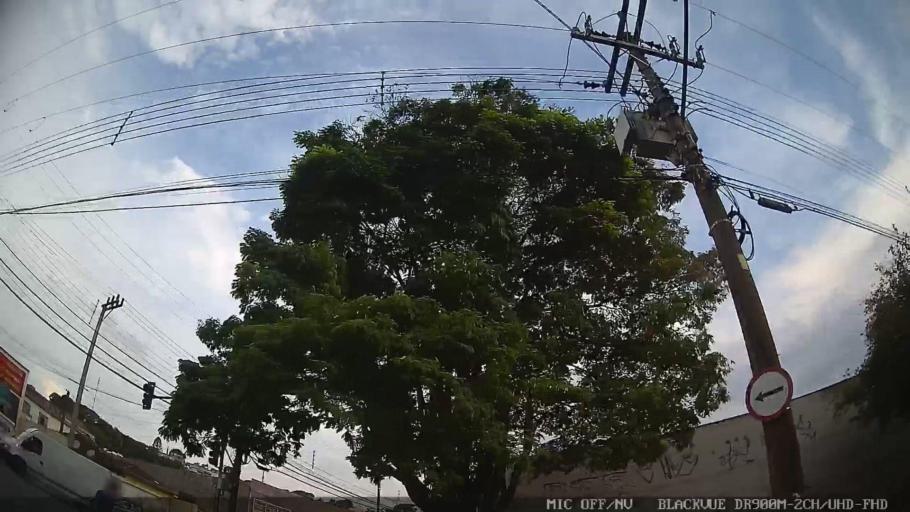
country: BR
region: Sao Paulo
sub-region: Braganca Paulista
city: Braganca Paulista
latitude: -22.9390
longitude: -46.5360
